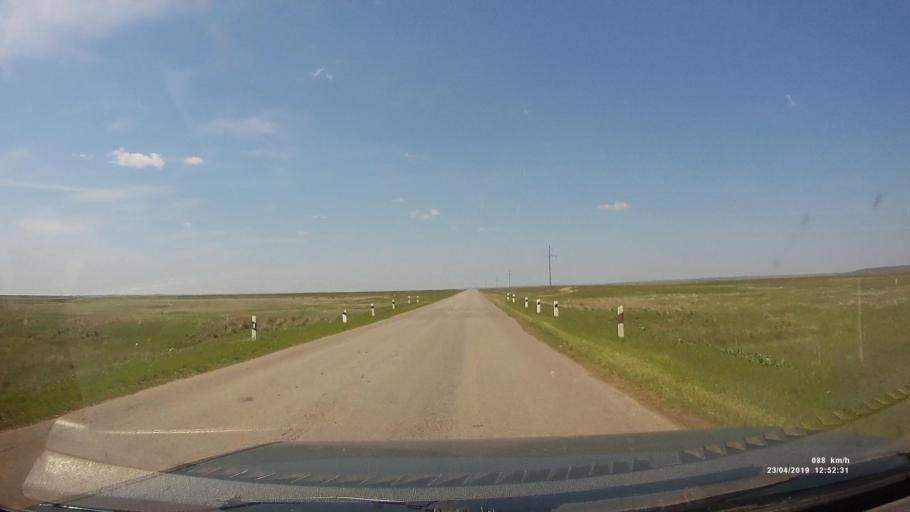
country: RU
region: Kalmykiya
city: Yashalta
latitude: 46.5653
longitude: 42.6086
